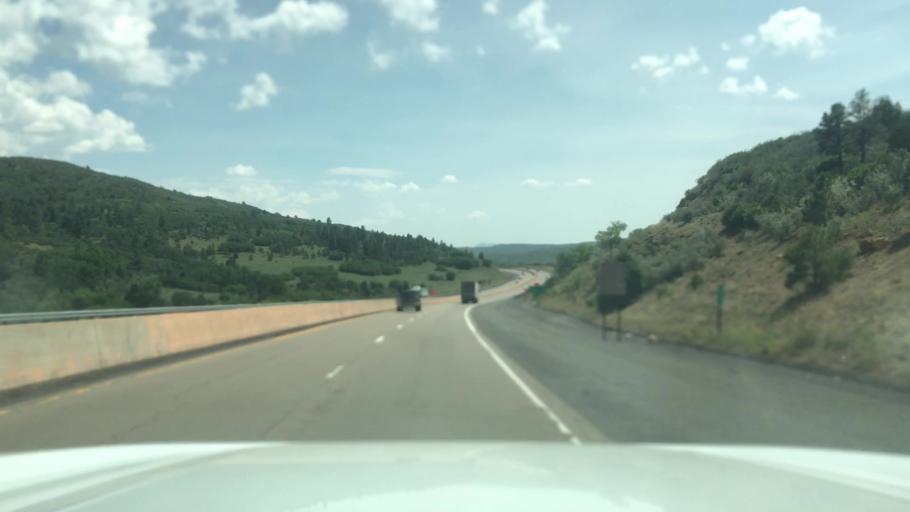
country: US
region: New Mexico
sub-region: Colfax County
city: Raton
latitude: 36.9728
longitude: -104.4784
